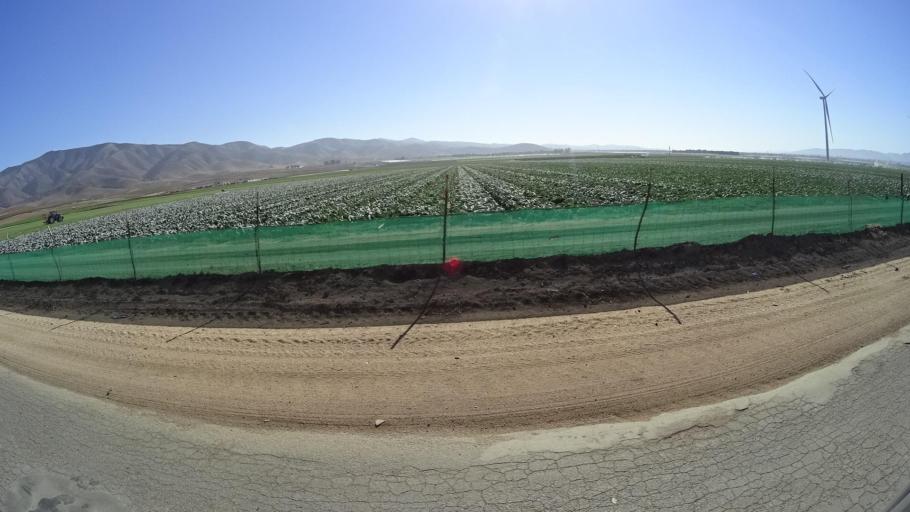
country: US
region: California
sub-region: Monterey County
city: Soledad
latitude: 36.4642
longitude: -121.3536
